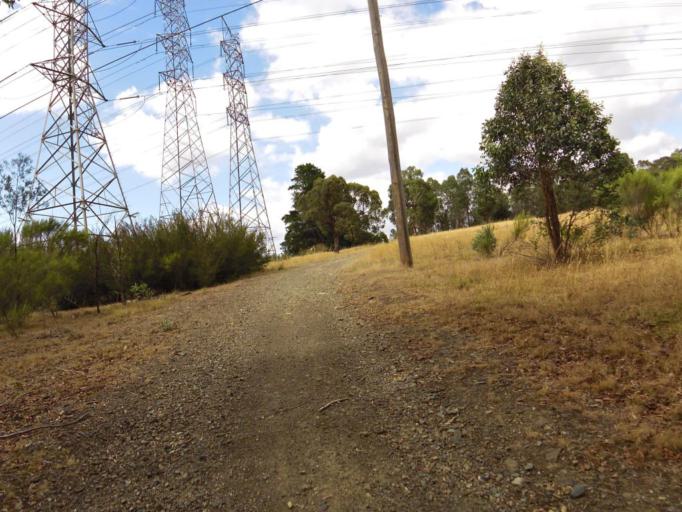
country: AU
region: Victoria
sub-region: Nillumbik
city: Eltham
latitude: -37.7416
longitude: 145.1454
